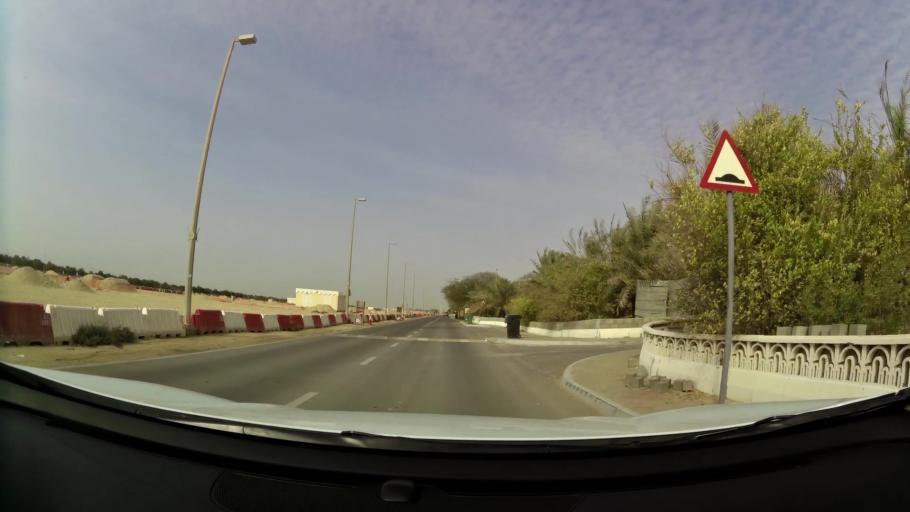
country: AE
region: Abu Dhabi
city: Abu Dhabi
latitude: 24.6062
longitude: 54.6993
